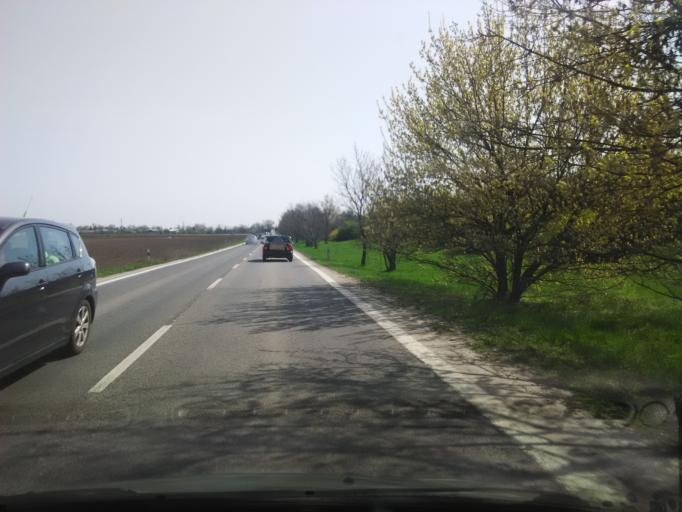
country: SK
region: Nitriansky
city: Sellye
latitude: 48.1572
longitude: 17.9118
